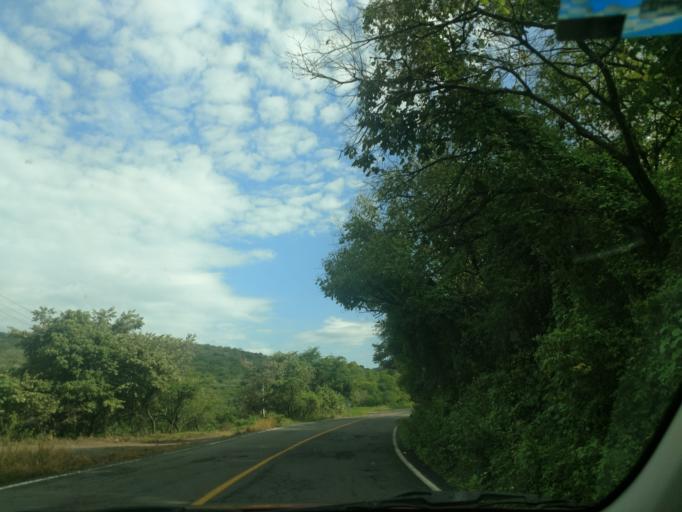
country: MX
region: Jalisco
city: Ameca
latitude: 20.5390
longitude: -104.1911
